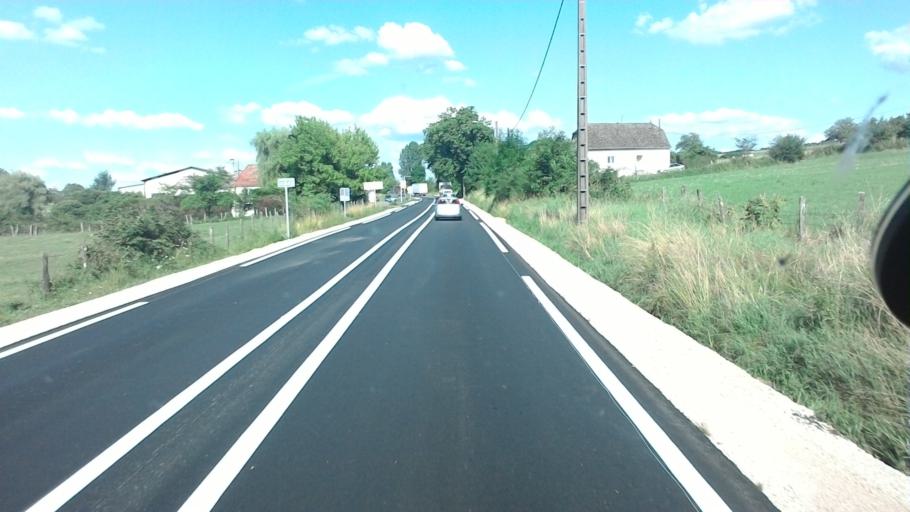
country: FR
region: Franche-Comte
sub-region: Departement de la Haute-Saone
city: Gy
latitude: 47.4254
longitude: 5.8456
